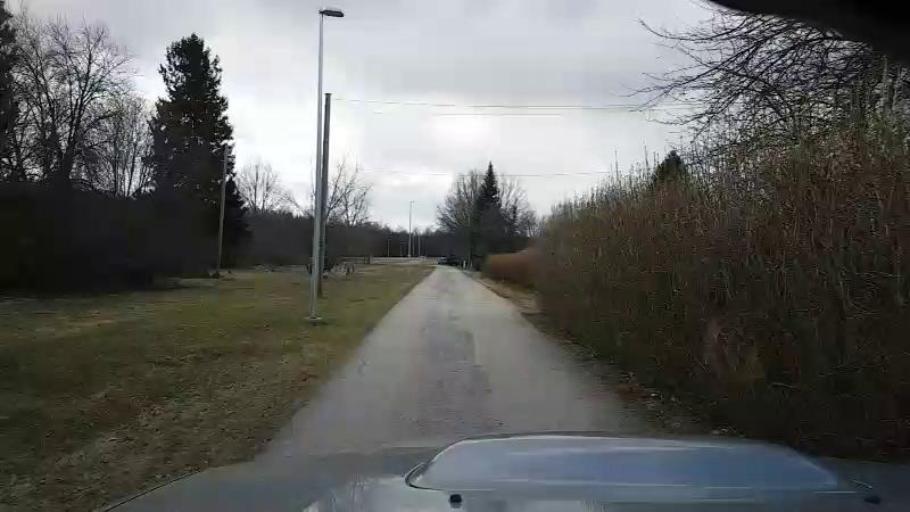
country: EE
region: Jaervamaa
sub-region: Paide linn
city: Paide
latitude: 58.9037
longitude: 25.5764
